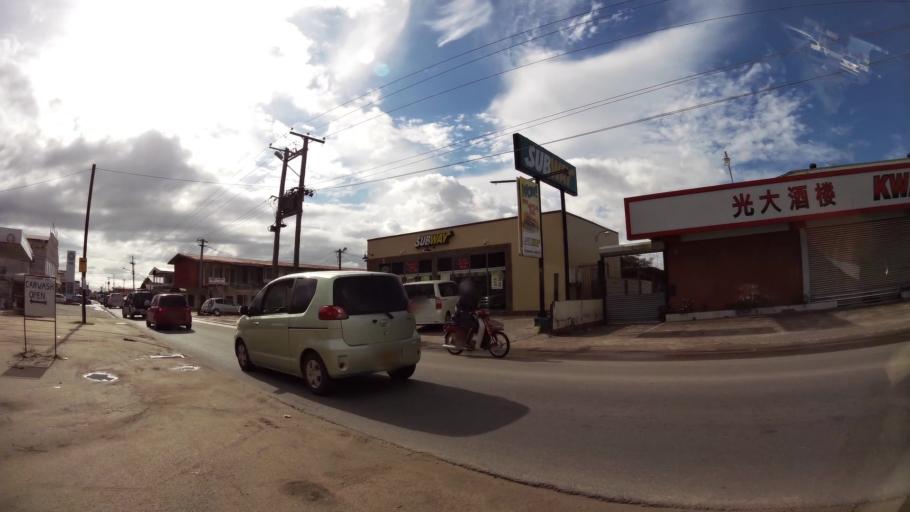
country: SR
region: Paramaribo
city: Paramaribo
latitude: 5.8430
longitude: -55.2122
